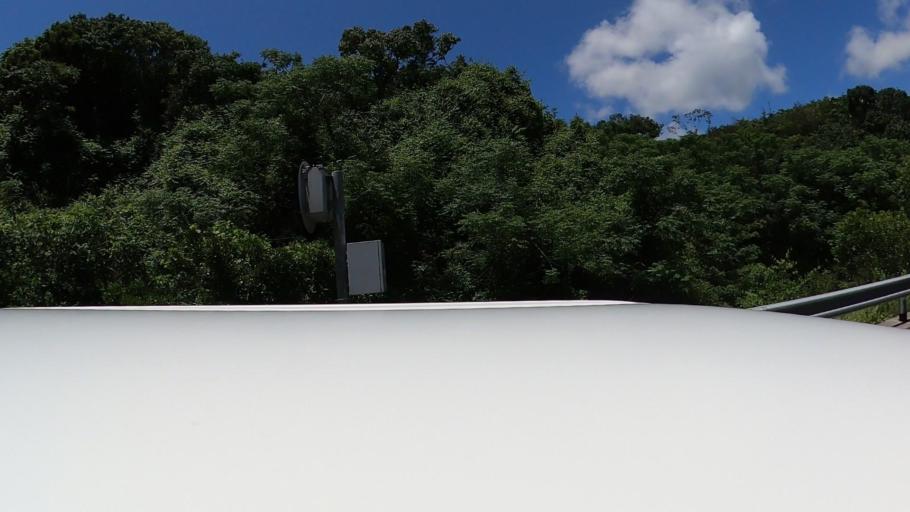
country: JP
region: Miyazaki
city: Nobeoka
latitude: 32.4878
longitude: 131.6454
